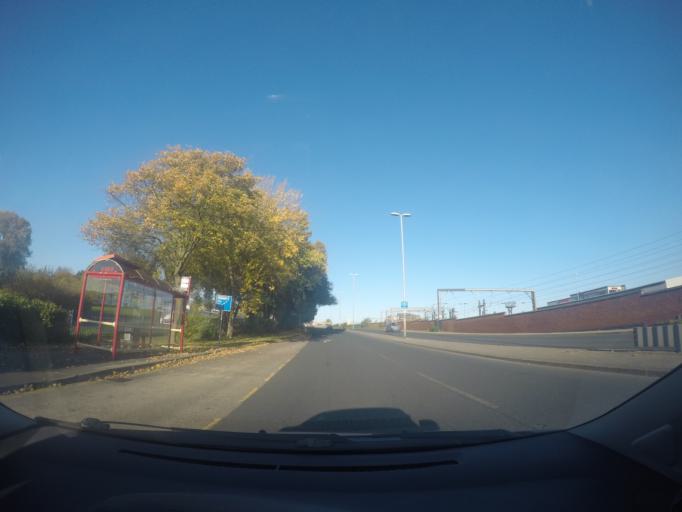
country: GB
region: England
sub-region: City and Borough of Leeds
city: Leeds
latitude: 53.7956
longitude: -1.5696
